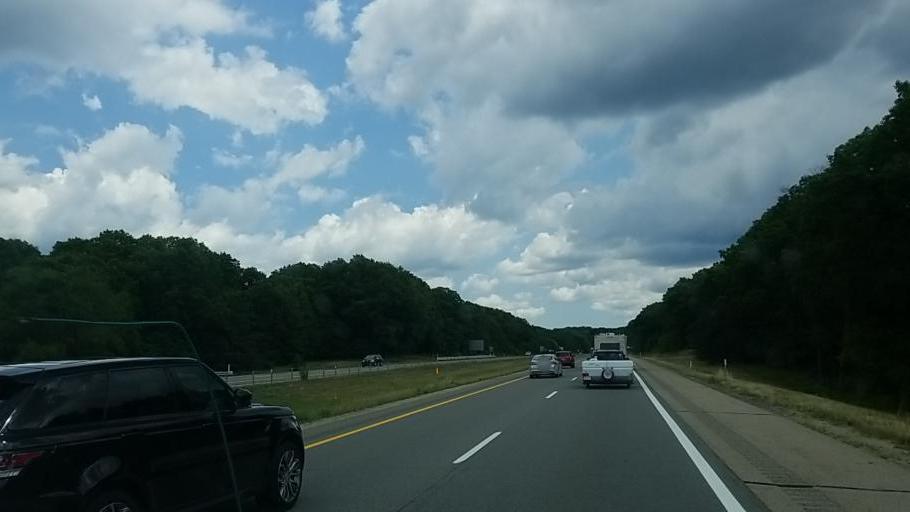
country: US
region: Michigan
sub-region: Kent County
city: Northview
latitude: 43.0164
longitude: -85.6248
